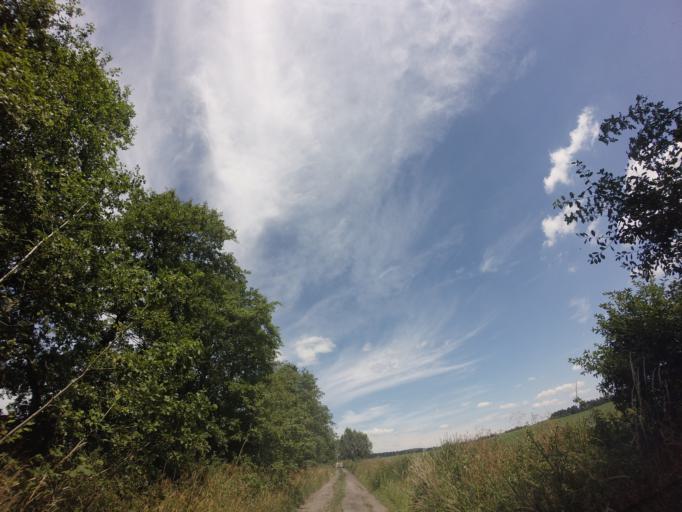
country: PL
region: West Pomeranian Voivodeship
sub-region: Powiat choszczenski
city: Recz
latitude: 53.2736
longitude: 15.5330
